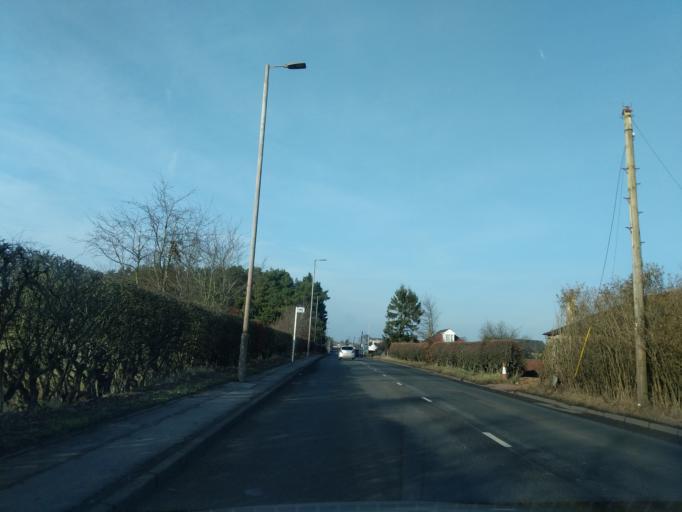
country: GB
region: Scotland
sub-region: South Lanarkshire
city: Carluke
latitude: 55.7189
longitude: -3.8325
